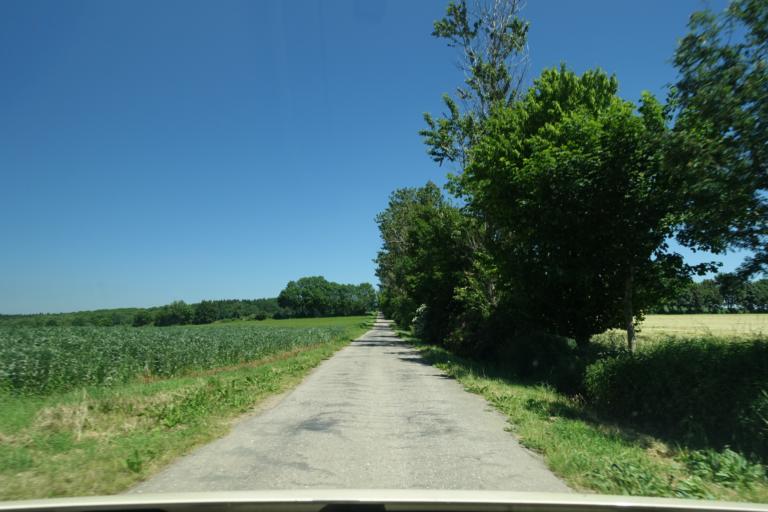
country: DE
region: Saxony
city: Eppendorf
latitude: 50.8232
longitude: 13.2538
